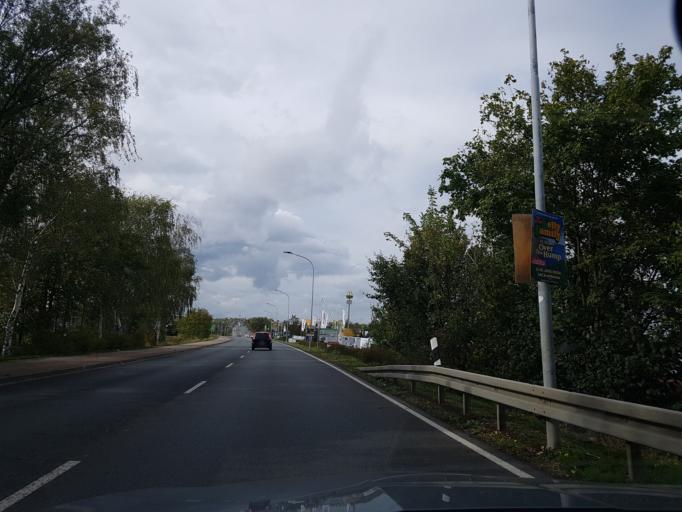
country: DE
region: Saxony
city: Riesa
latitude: 51.2942
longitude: 13.2889
